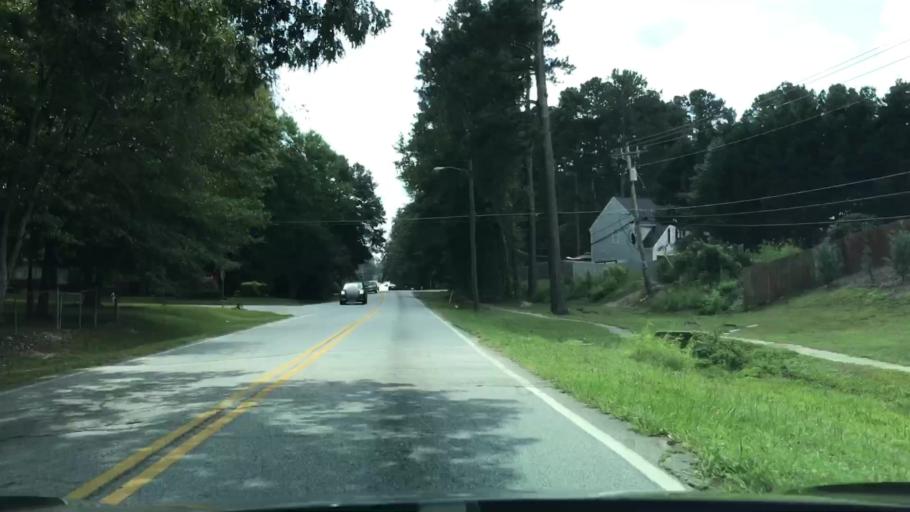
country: US
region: Georgia
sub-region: Gwinnett County
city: Lawrenceville
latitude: 33.9453
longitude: -84.0626
